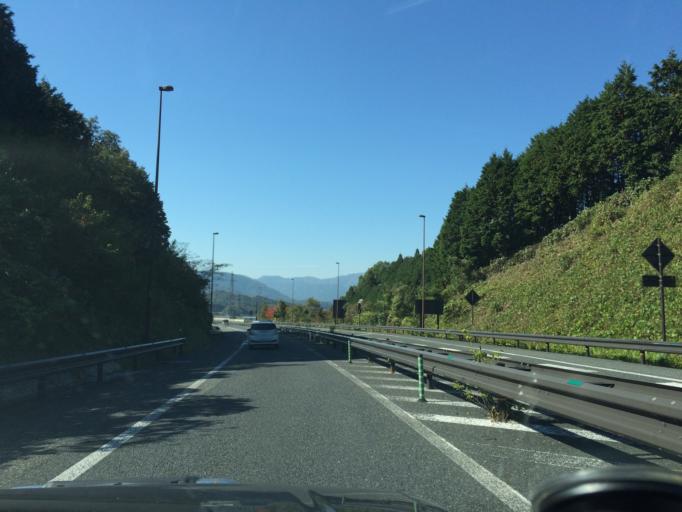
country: JP
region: Kyoto
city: Fukuchiyama
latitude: 35.3042
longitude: 134.9161
